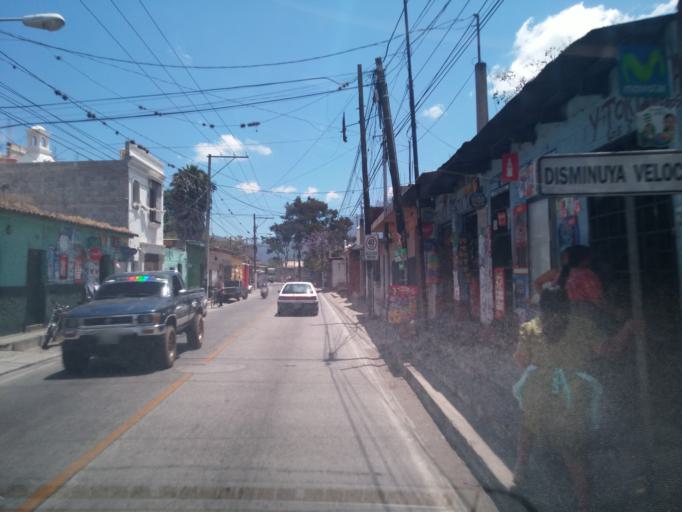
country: GT
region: Sacatepequez
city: Jocotenango
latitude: 14.5816
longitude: -90.7442
